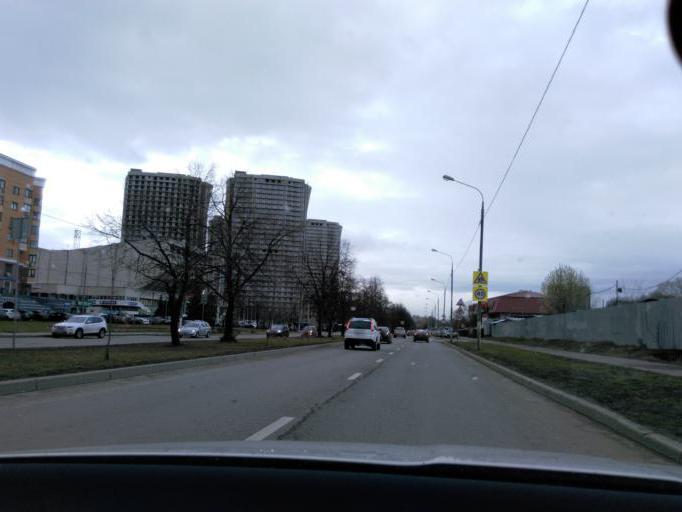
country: RU
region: Moscow
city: Golovinskiy
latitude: 55.8566
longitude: 37.4918
